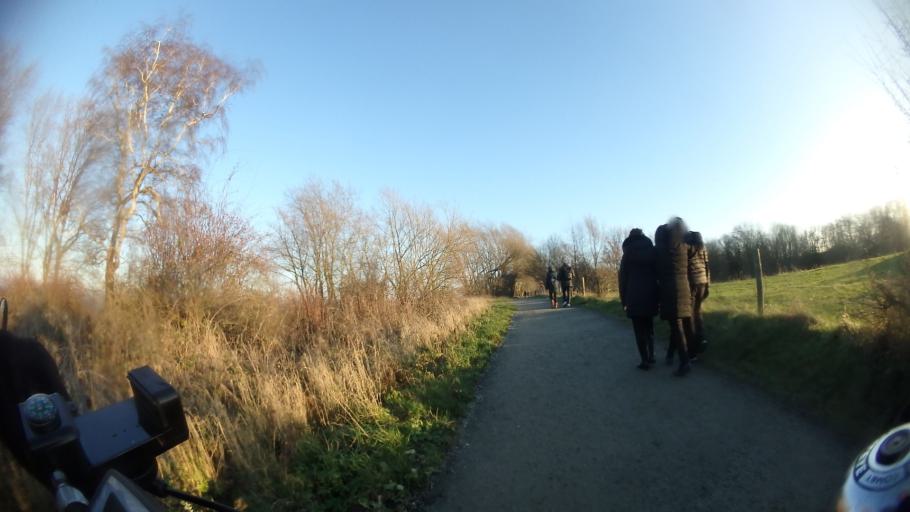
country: DE
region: Schleswig-Holstein
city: Travemuende
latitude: 53.9902
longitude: 10.8695
